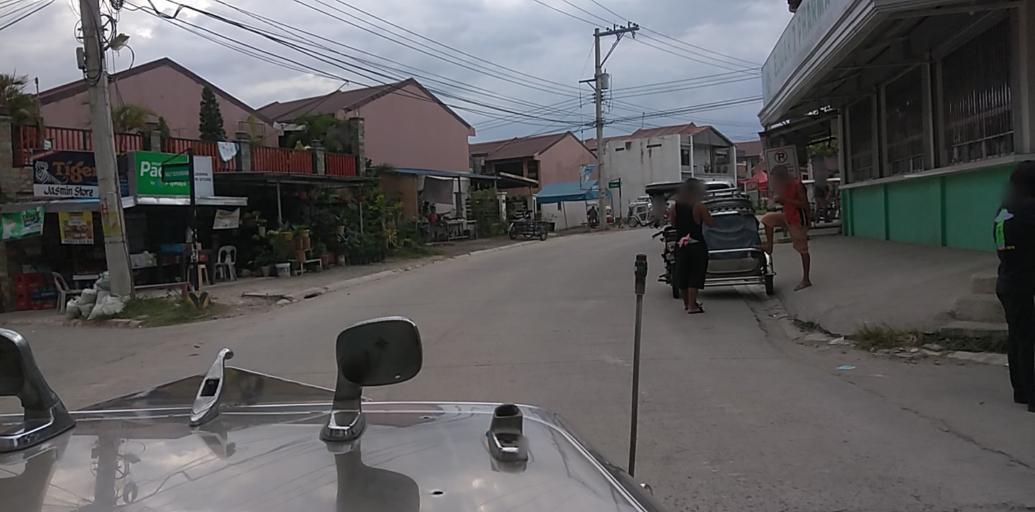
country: PH
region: Central Luzon
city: Santol
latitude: 15.1665
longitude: 120.5348
